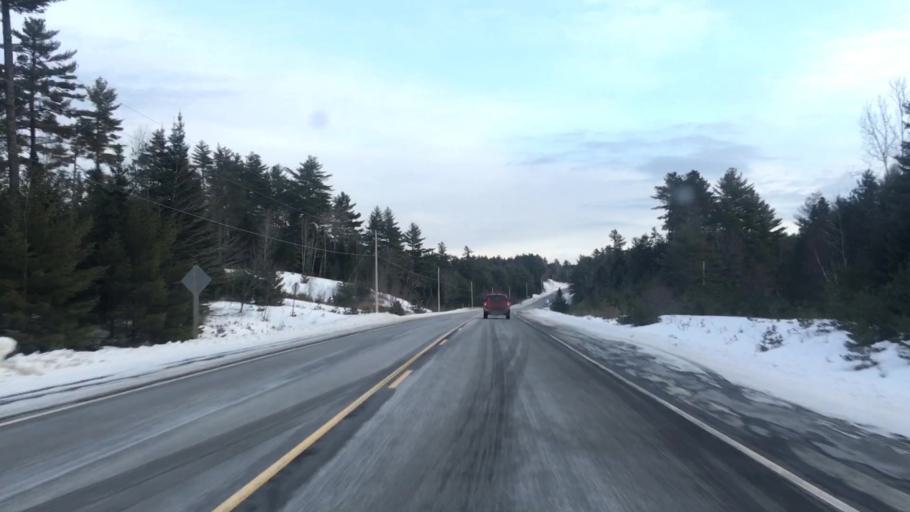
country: US
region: Maine
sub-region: Washington County
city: Addison
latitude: 44.9352
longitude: -67.7383
